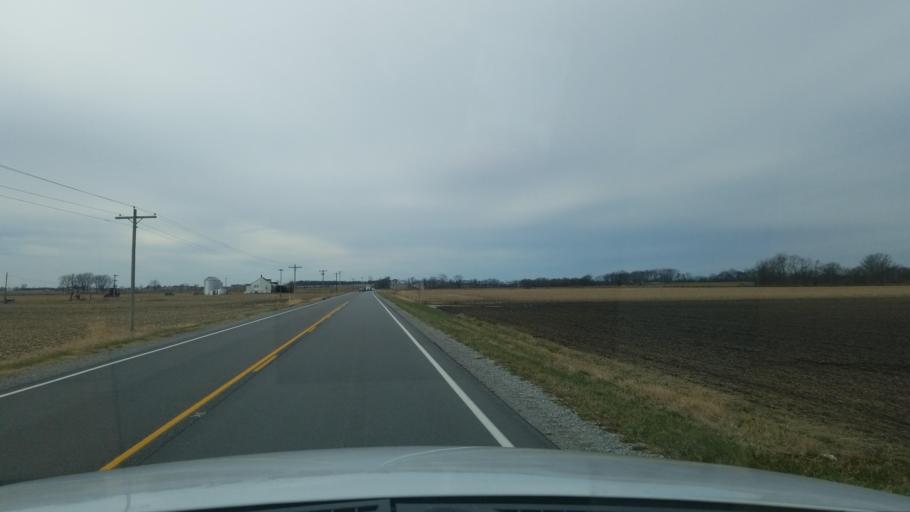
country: US
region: Illinois
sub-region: White County
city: Norris City
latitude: 37.9076
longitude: -88.1665
